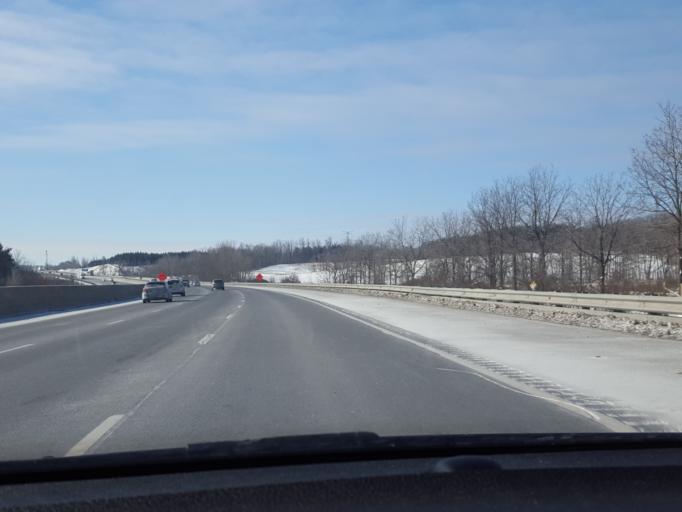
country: CA
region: Ontario
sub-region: Halton
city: Milton
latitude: 43.5130
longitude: -79.9484
